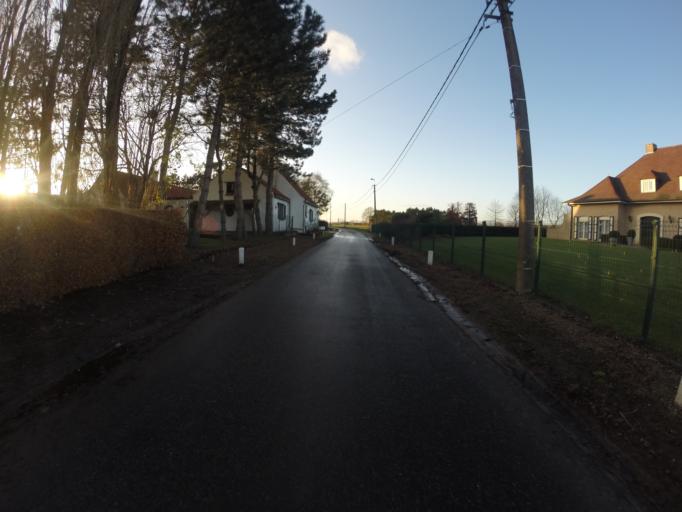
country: BE
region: Flanders
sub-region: Provincie Oost-Vlaanderen
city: Nevele
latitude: 51.0381
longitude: 3.4912
